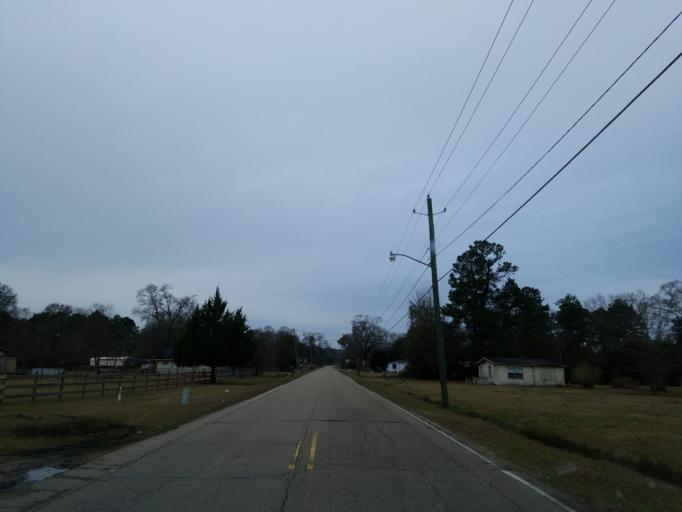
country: US
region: Mississippi
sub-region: Forrest County
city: Hattiesburg
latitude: 31.2886
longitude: -89.2632
